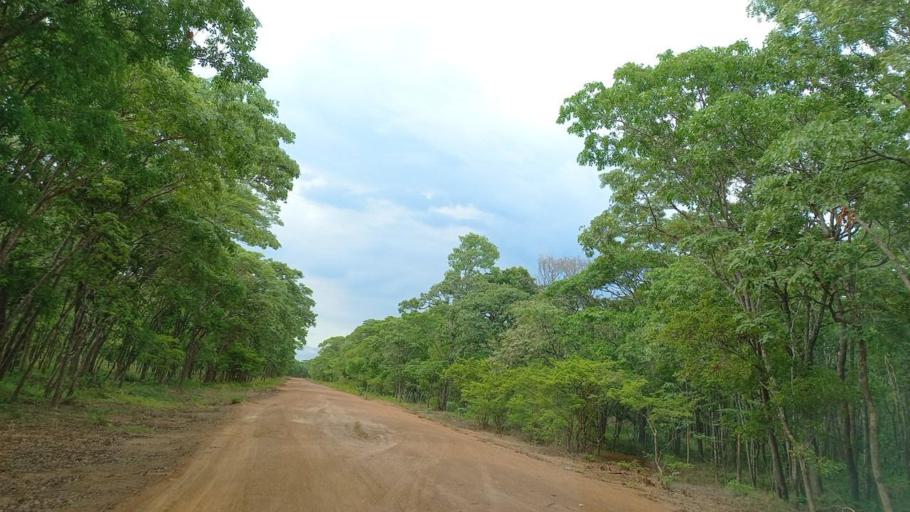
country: ZM
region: North-Western
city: Kalengwa
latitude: -13.3875
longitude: 25.0709
